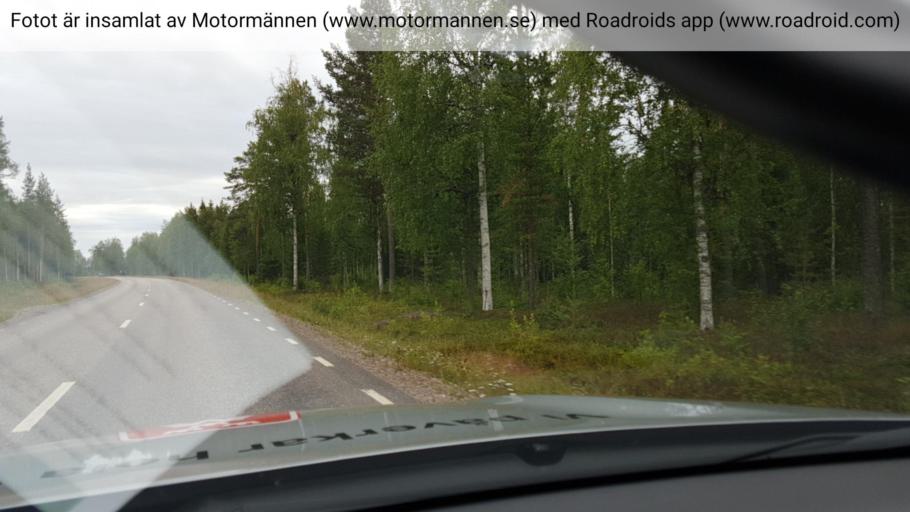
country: SE
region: Norrbotten
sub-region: Overkalix Kommun
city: OEverkalix
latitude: 66.5069
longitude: 22.7643
